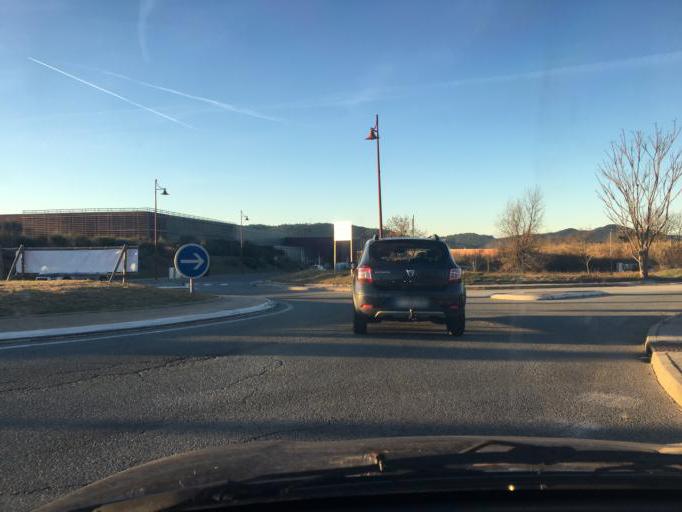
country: FR
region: Provence-Alpes-Cote d'Azur
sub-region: Departement du Var
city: Les Arcs
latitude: 43.4528
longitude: 6.4897
